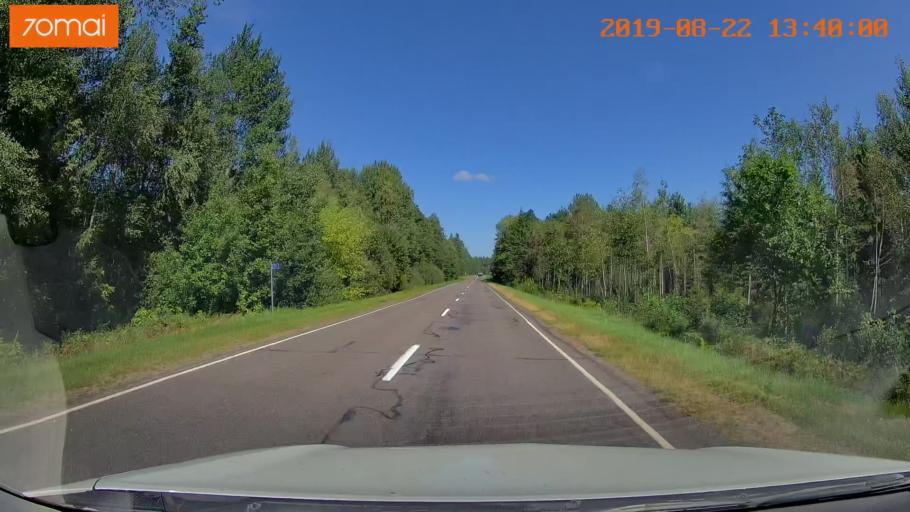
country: BY
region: Minsk
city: Staryya Darohi
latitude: 53.2316
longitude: 28.3591
